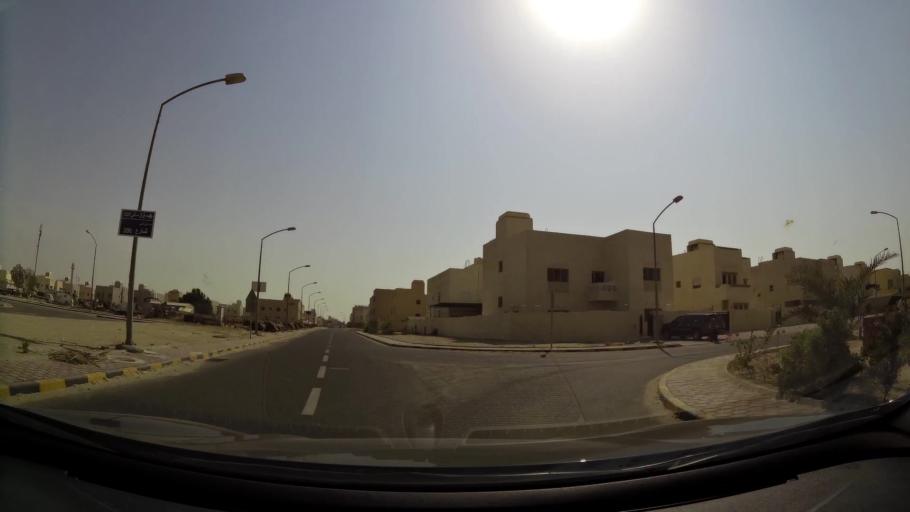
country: KW
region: Al Ahmadi
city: Al Wafrah
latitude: 28.8086
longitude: 48.0530
